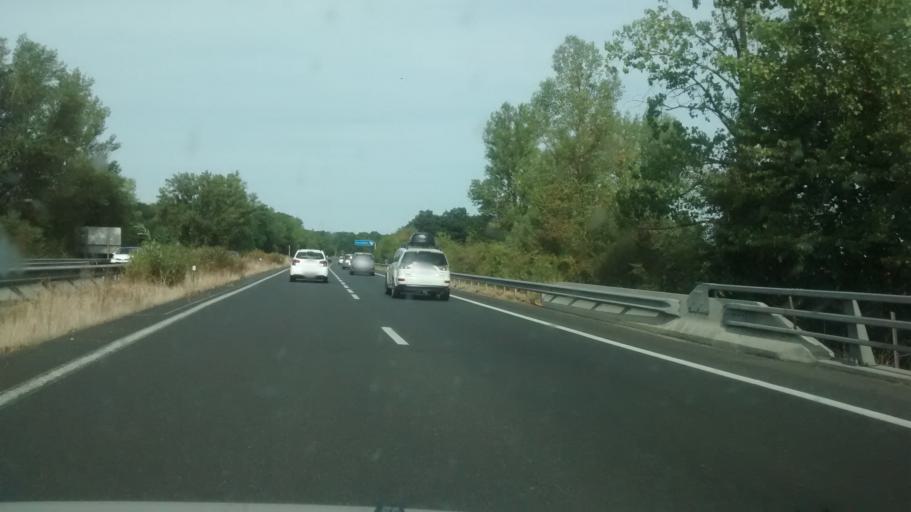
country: FR
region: Aquitaine
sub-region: Departement de la Gironde
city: Gironde-sur-Dropt
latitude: 44.5144
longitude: -0.0732
